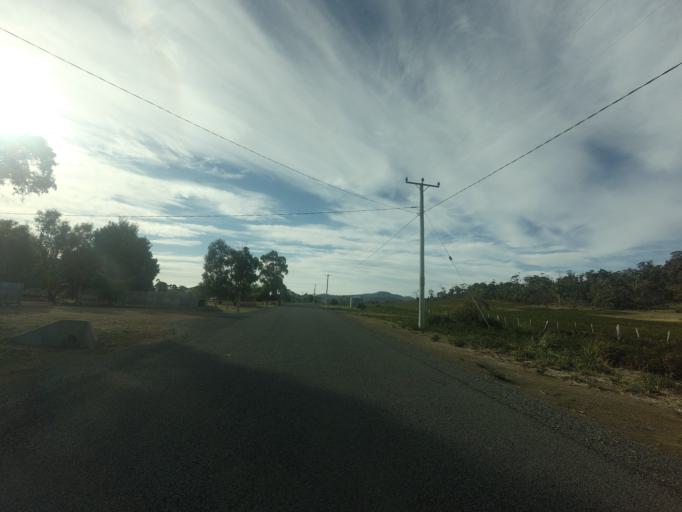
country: AU
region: Tasmania
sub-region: Sorell
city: Sorell
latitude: -42.9691
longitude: 147.8318
